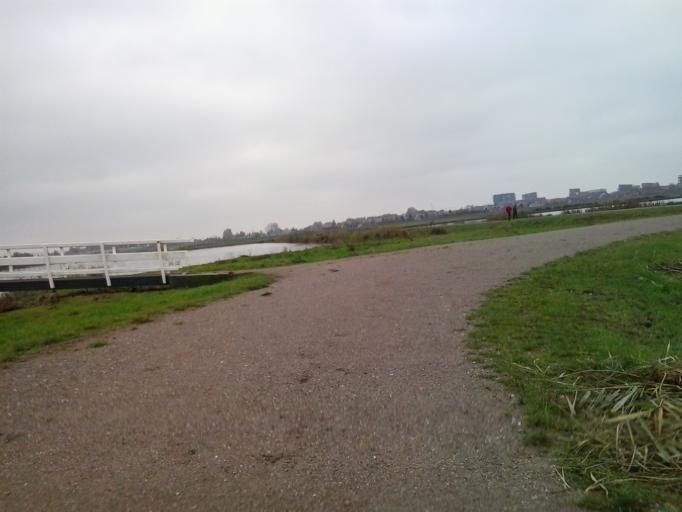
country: NL
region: South Holland
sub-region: Gemeente Lansingerland
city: Berkel en Rodenrijs
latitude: 52.0049
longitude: 4.4663
